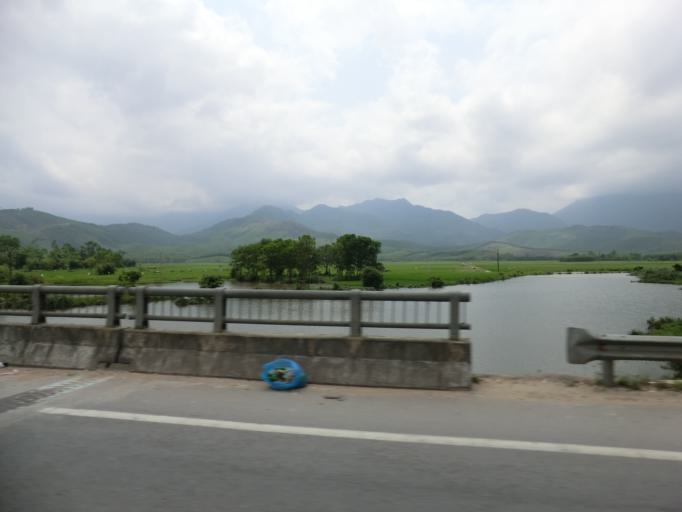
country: VN
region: Thua Thien-Hue
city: Phu Loc
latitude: 16.2690
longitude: 107.8946
